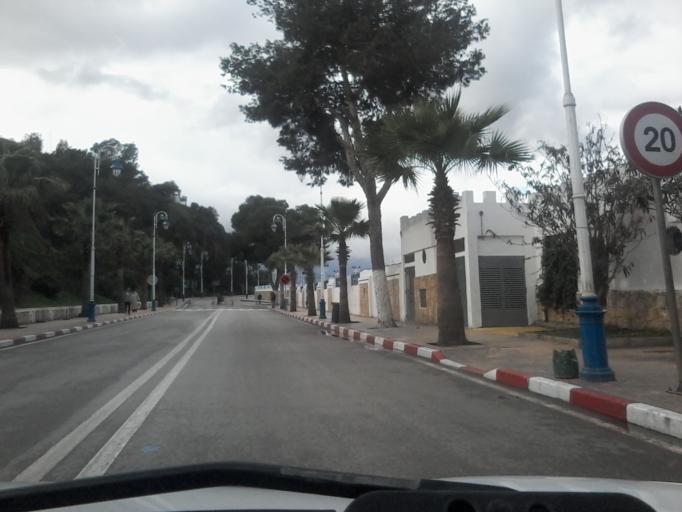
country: MA
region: Tanger-Tetouan
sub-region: Tetouan
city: Martil
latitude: 35.6812
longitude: -5.3128
